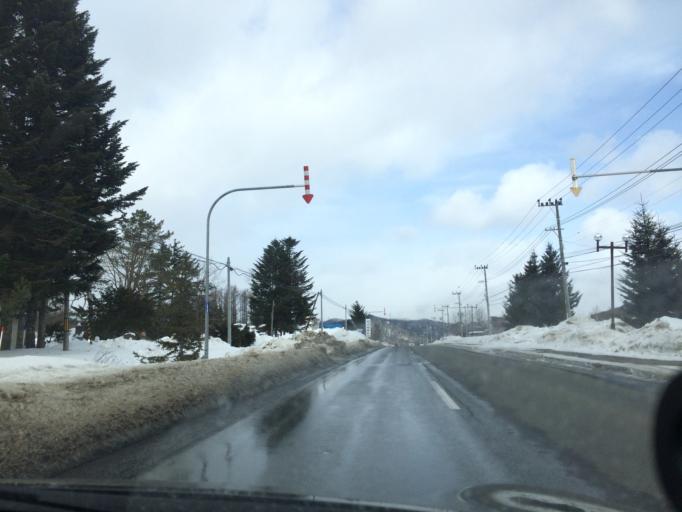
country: JP
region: Hokkaido
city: Shimo-furano
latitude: 42.9878
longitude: 142.3983
